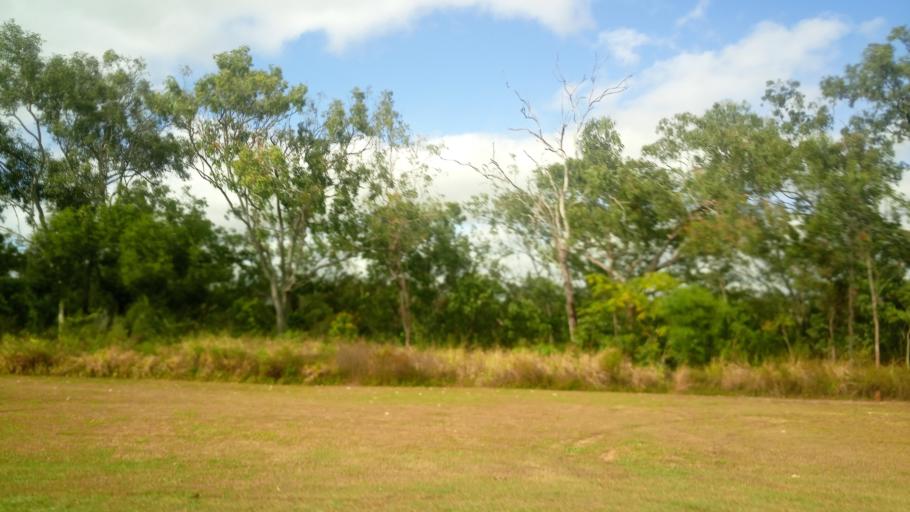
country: AU
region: Queensland
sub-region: Tablelands
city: Mareeba
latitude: -16.9763
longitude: 145.4589
